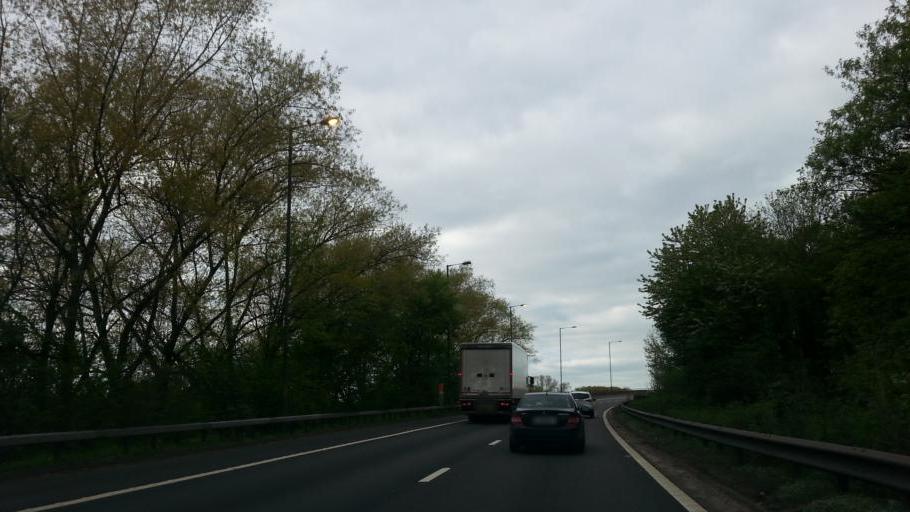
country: GB
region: England
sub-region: Sandwell
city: West Bromwich
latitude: 52.5391
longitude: -1.9695
